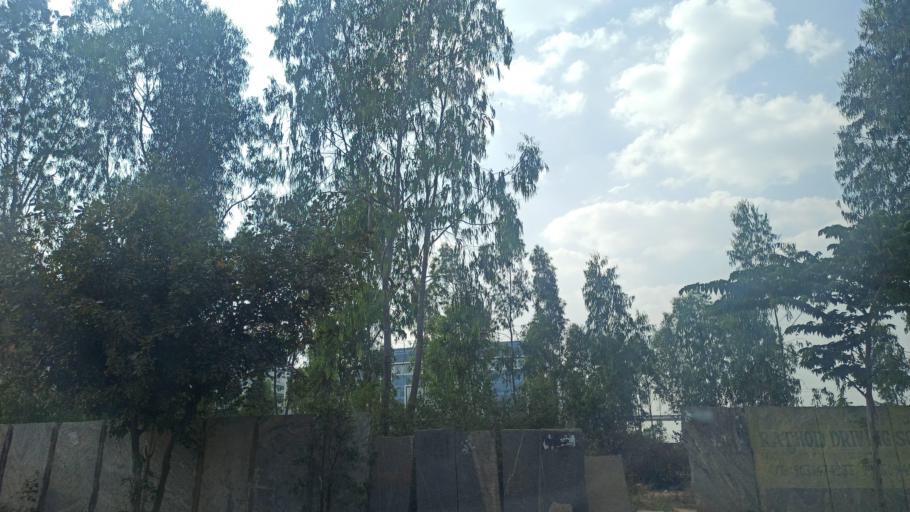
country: IN
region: Karnataka
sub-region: Bangalore Urban
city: Yelahanka
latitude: 13.1161
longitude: 77.6092
